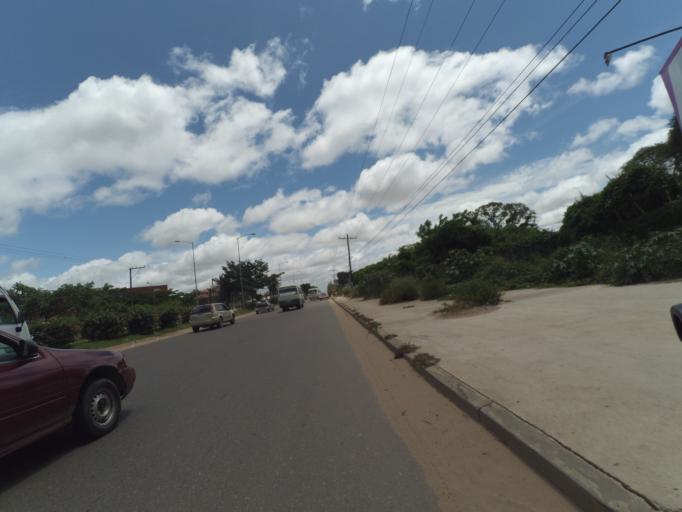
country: BO
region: Santa Cruz
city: Santa Cruz de la Sierra
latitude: -17.8363
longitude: -63.2358
